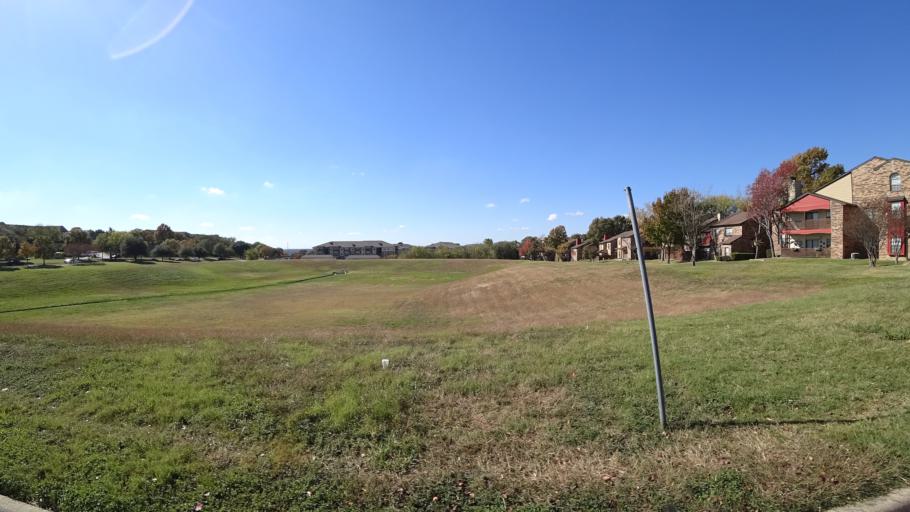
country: US
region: Texas
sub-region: Travis County
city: Wells Branch
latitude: 30.4426
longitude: -97.6925
